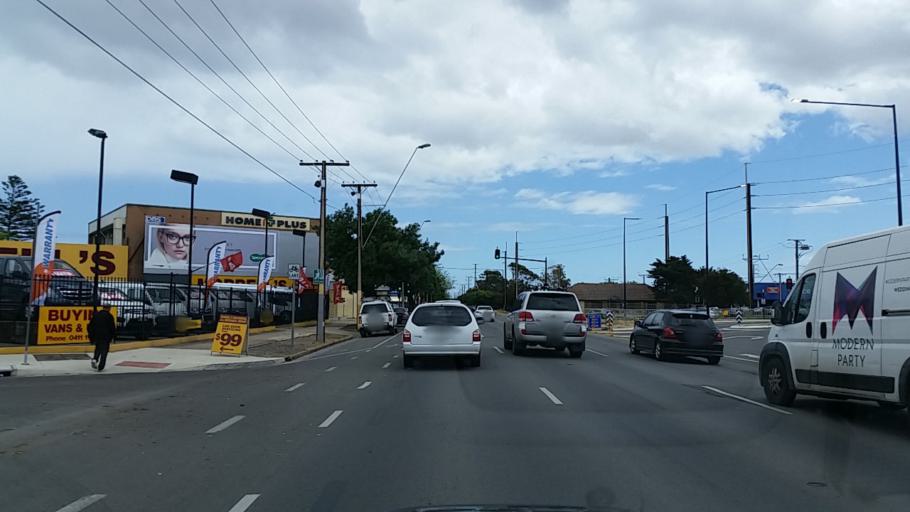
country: AU
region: South Australia
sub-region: Charles Sturt
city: Allenby Gardens
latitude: -34.8998
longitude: 138.5634
